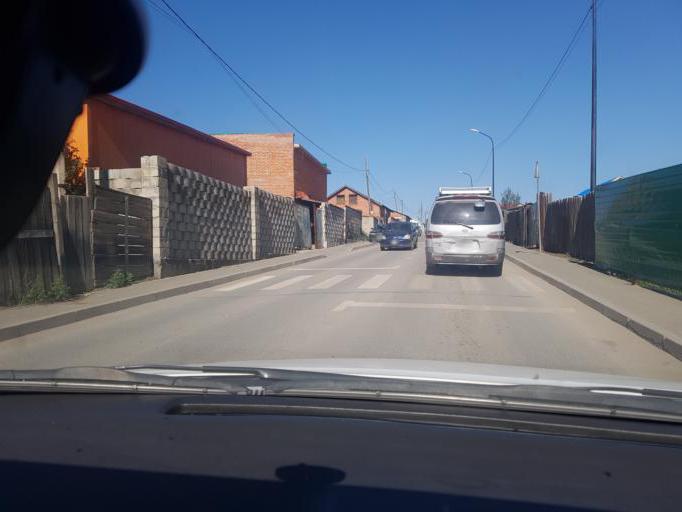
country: MN
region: Ulaanbaatar
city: Ulaanbaatar
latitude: 47.9499
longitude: 106.8638
